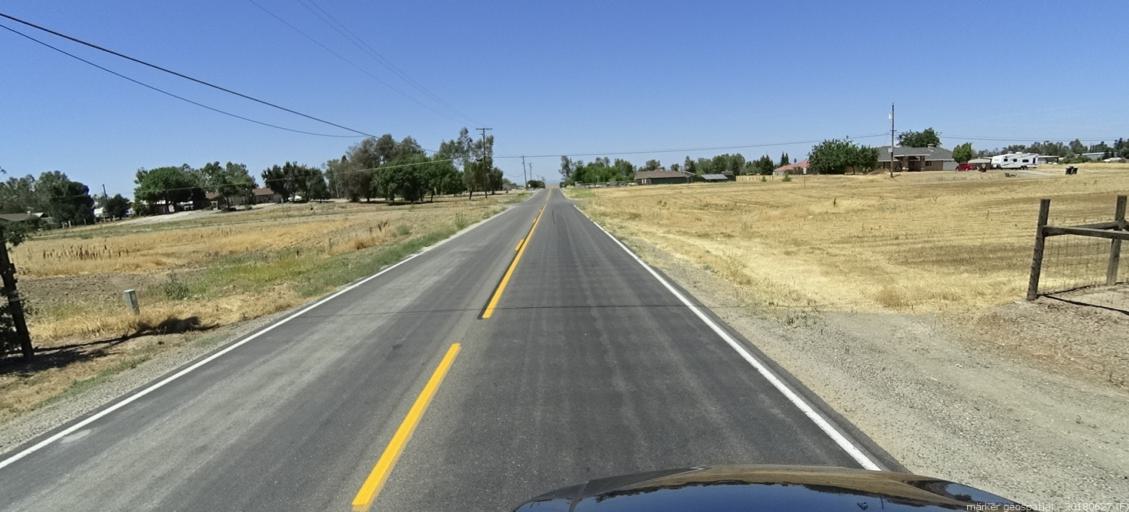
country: US
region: California
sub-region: Madera County
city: Bonadelle Ranchos-Madera Ranchos
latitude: 36.9611
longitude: -119.9120
